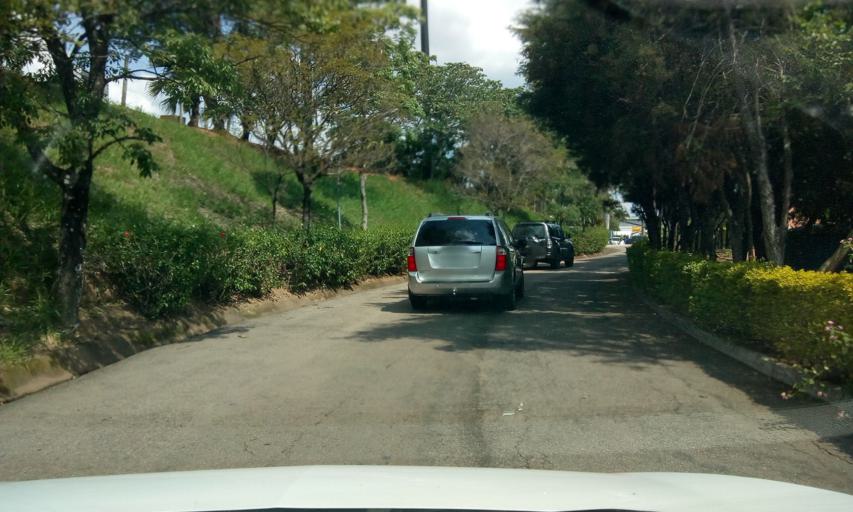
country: BR
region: Sao Paulo
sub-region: Louveira
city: Louveira
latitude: -23.1053
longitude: -47.0096
